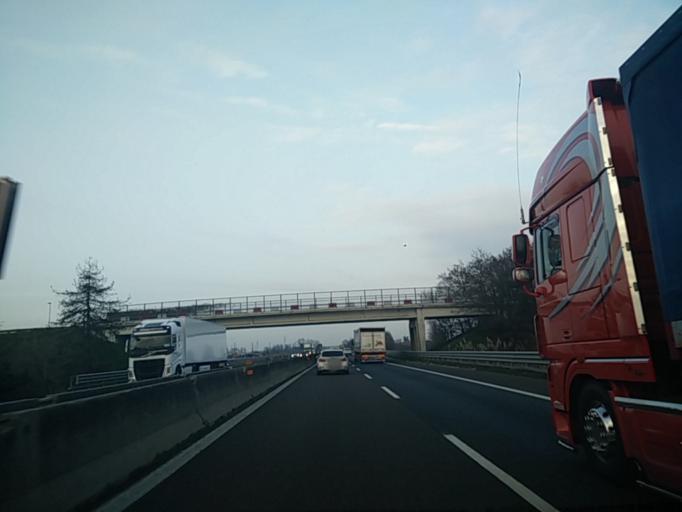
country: IT
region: Emilia-Romagna
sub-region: Provincia di Bologna
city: Progresso
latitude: 44.5627
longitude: 11.3813
